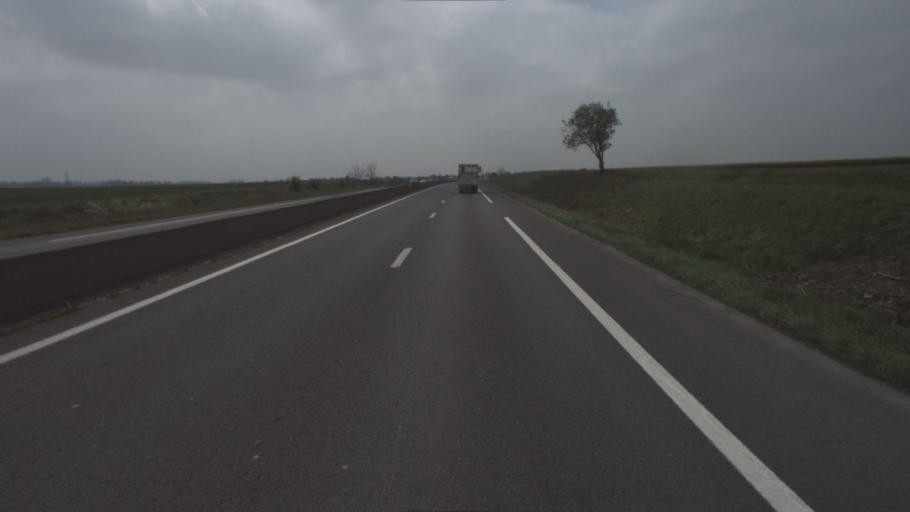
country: FR
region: Ile-de-France
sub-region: Departement de Seine-et-Marne
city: Mitry-Mory
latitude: 49.0076
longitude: 2.6482
